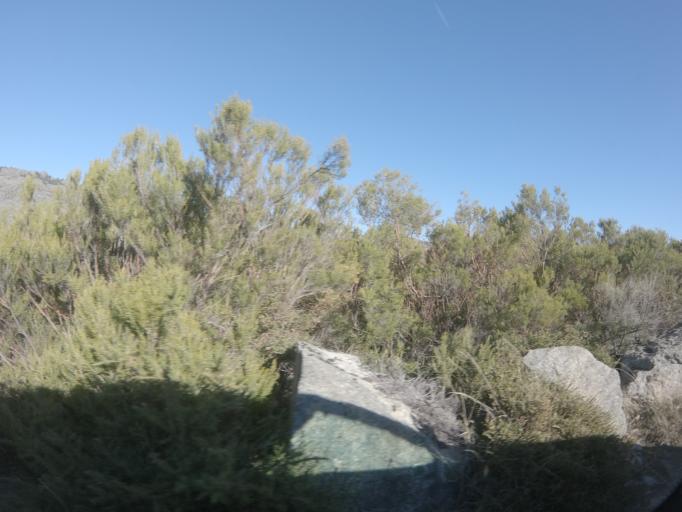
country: PT
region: Vila Real
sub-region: Vila Real
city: Vila Real
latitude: 41.3325
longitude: -7.8079
